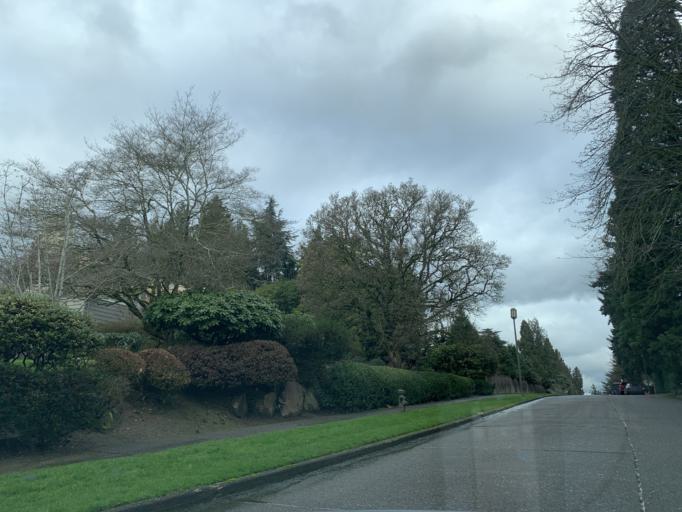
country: US
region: Washington
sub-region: King County
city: Yarrow Point
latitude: 47.6674
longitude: -122.2618
